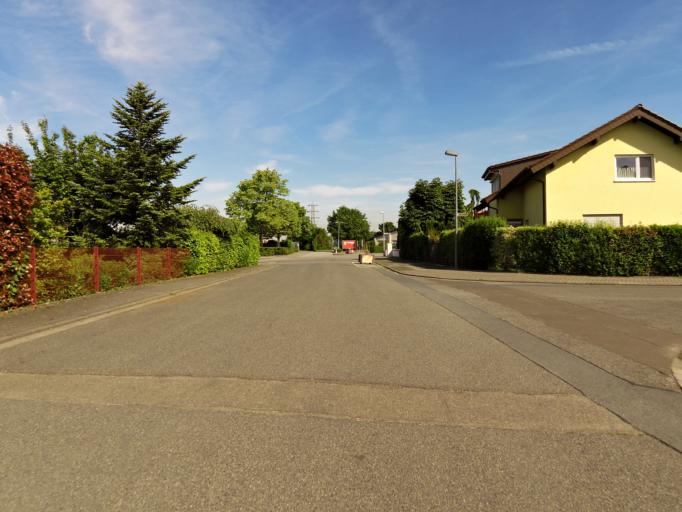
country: DE
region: Hesse
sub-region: Regierungsbezirk Darmstadt
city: Burstadt
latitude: 49.6657
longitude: 8.4442
